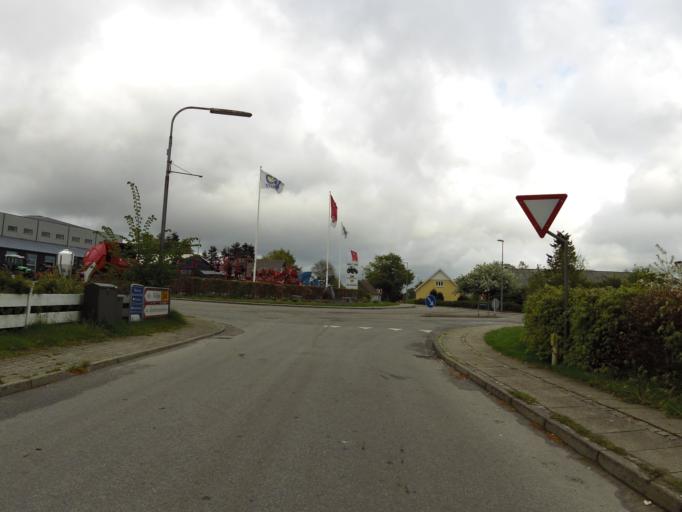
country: DK
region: South Denmark
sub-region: Haderslev Kommune
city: Gram
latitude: 55.2741
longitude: 9.0061
